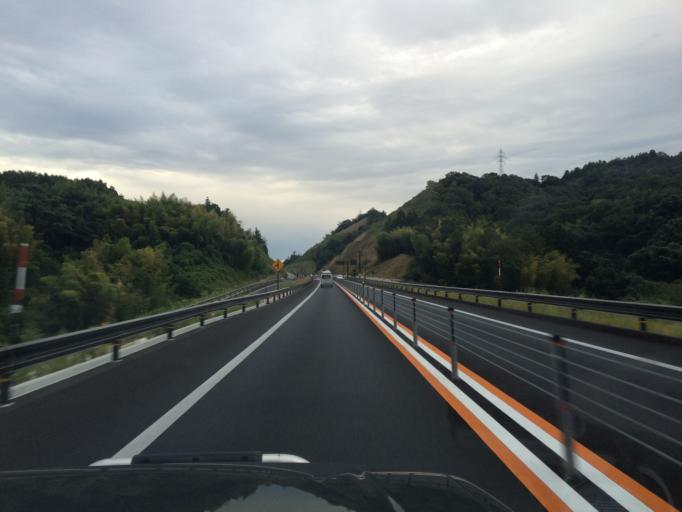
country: JP
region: Tottori
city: Tottori
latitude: 35.4934
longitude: 134.1350
